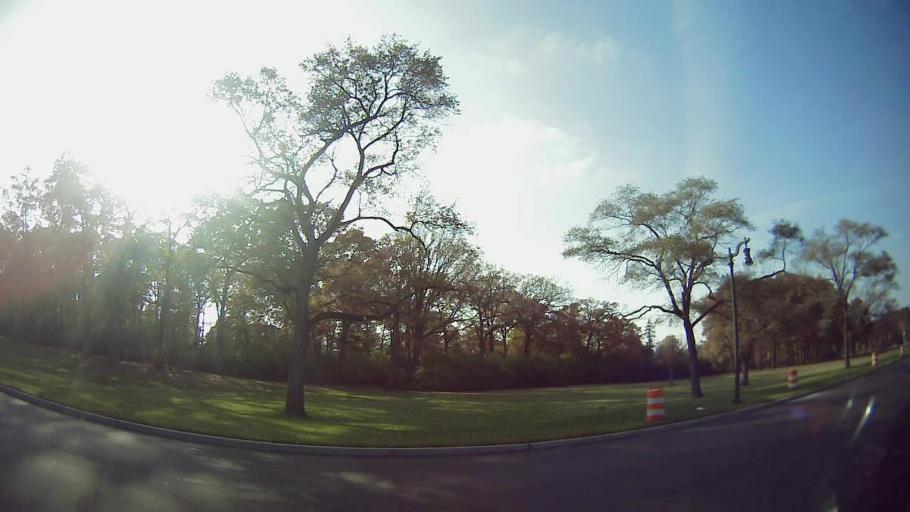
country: US
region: Michigan
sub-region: Oakland County
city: Ferndale
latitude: 42.4285
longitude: -83.1238
